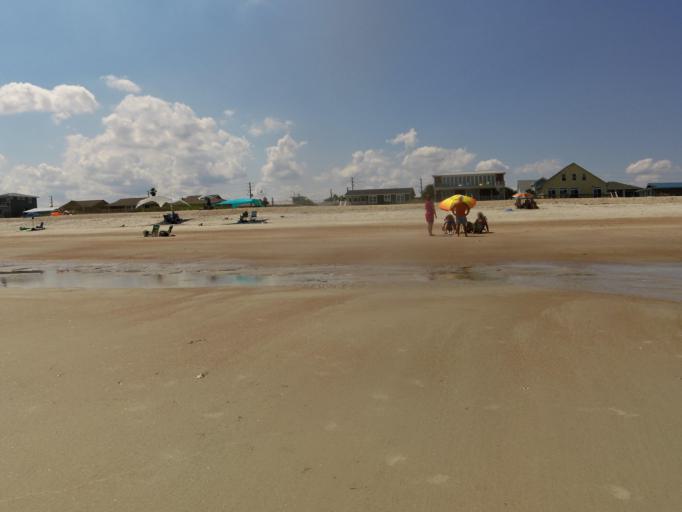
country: US
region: Florida
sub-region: Nassau County
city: Fernandina Beach
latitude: 30.6557
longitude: -81.4318
